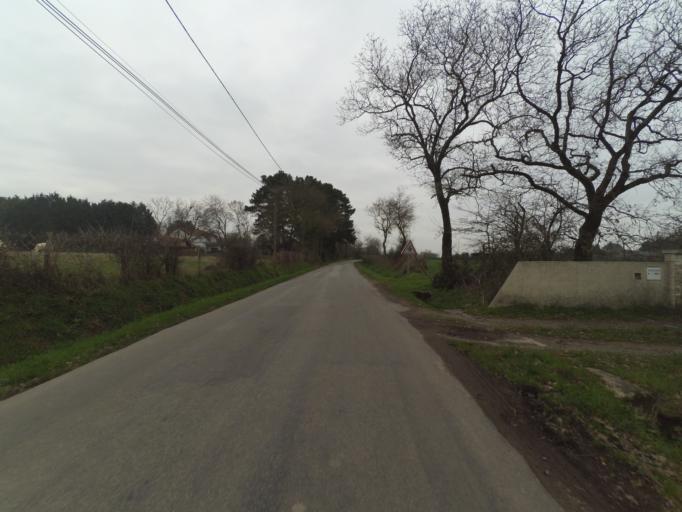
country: FR
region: Pays de la Loire
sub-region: Departement de la Loire-Atlantique
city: Sautron
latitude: 47.2536
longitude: -1.7074
